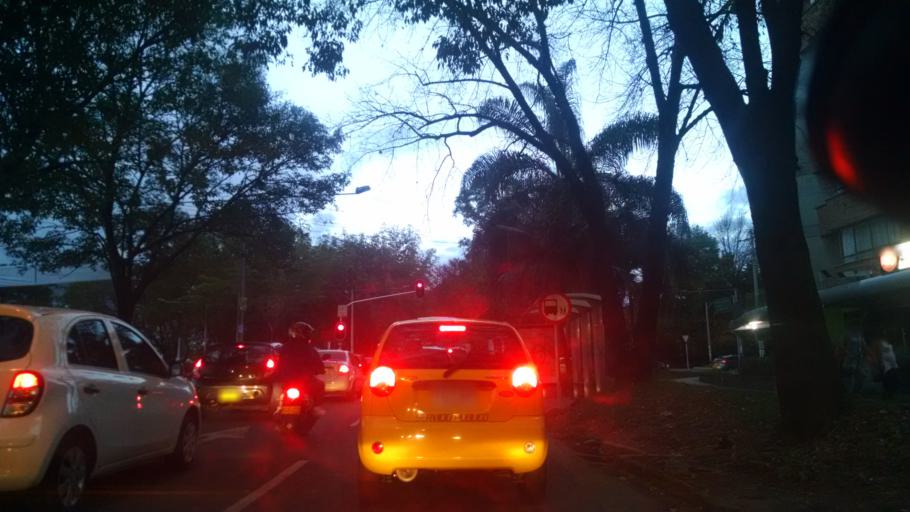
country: CO
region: Antioquia
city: Itagui
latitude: 6.2114
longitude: -75.5954
